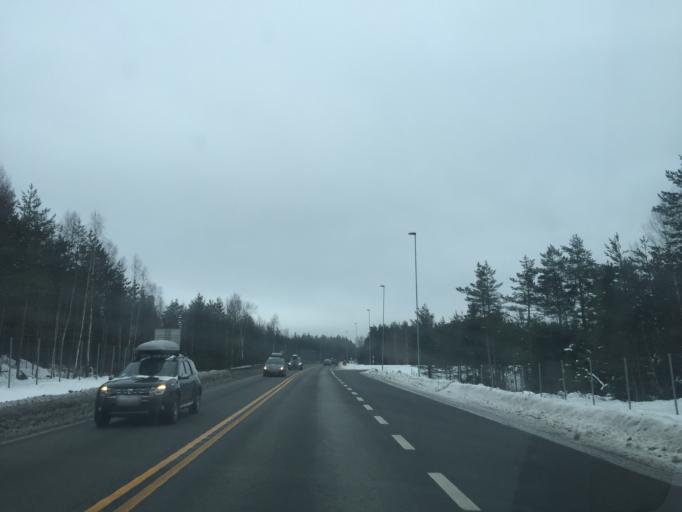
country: NO
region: Hedmark
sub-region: Stange
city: Stange
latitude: 60.7118
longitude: 11.2813
